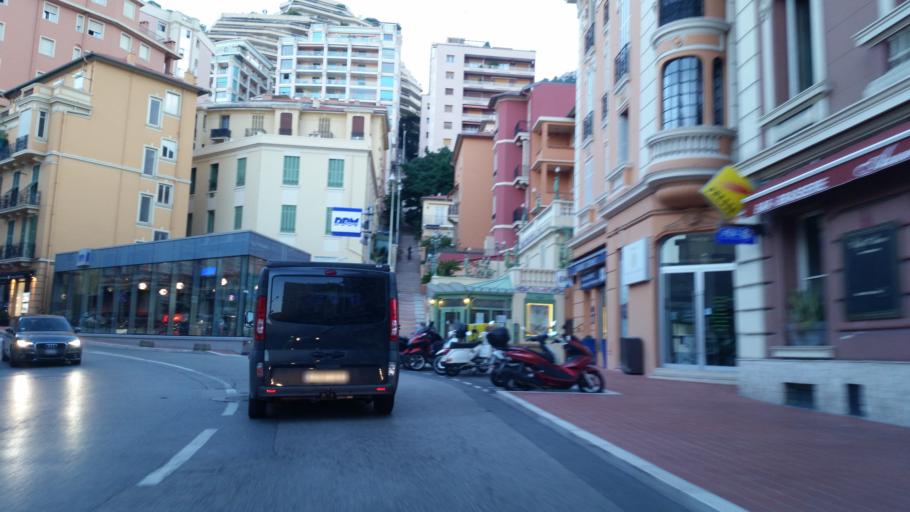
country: MC
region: Commune de Monaco
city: Moneghetti
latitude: 43.7370
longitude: 7.4166
